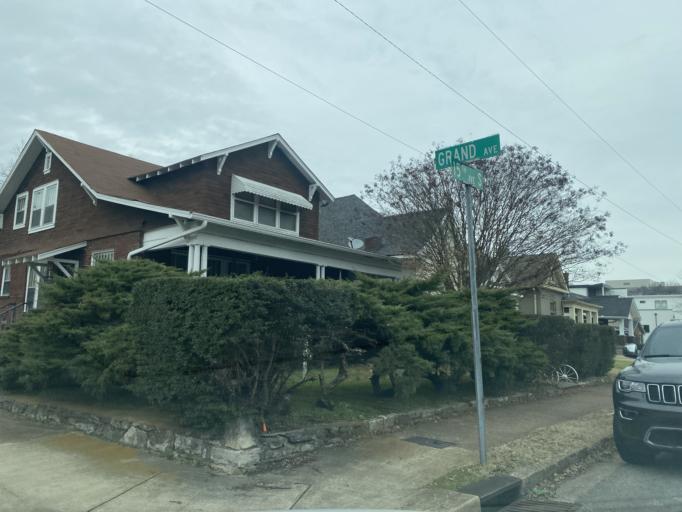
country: US
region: Tennessee
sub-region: Davidson County
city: Nashville
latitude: 36.1466
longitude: -86.7902
